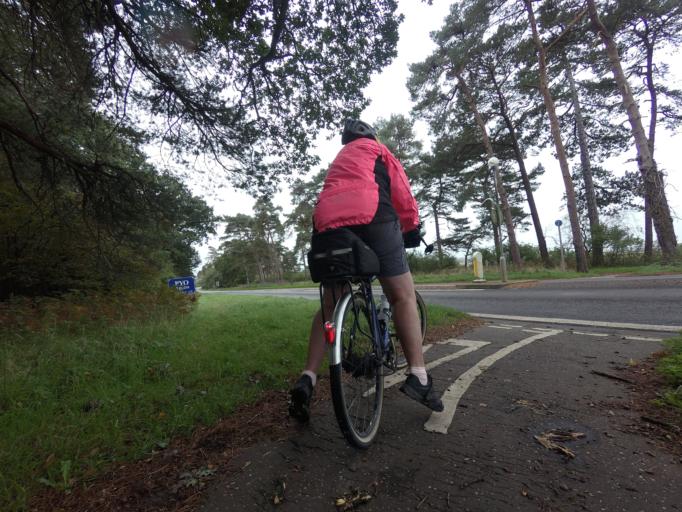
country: GB
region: England
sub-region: Norfolk
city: Dersingham
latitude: 52.8118
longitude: 0.4839
